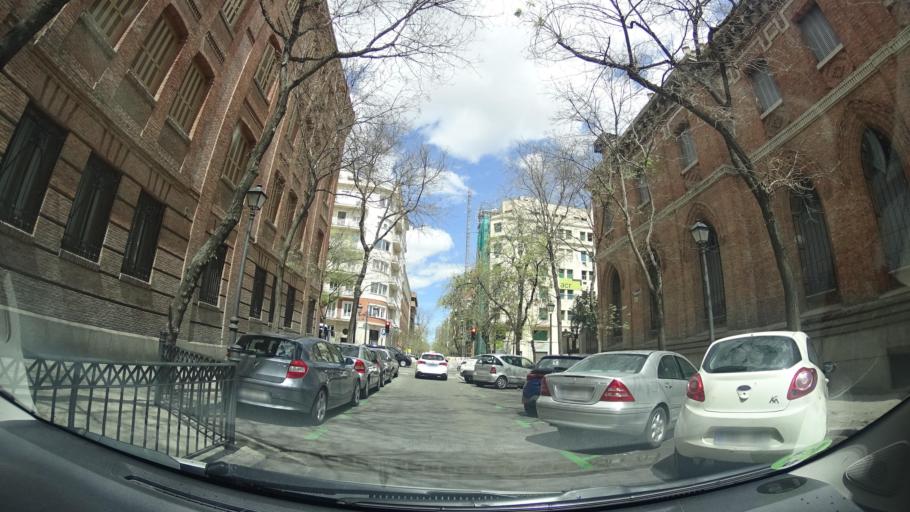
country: ES
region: Madrid
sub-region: Provincia de Madrid
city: Chamberi
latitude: 40.4324
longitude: -3.6950
